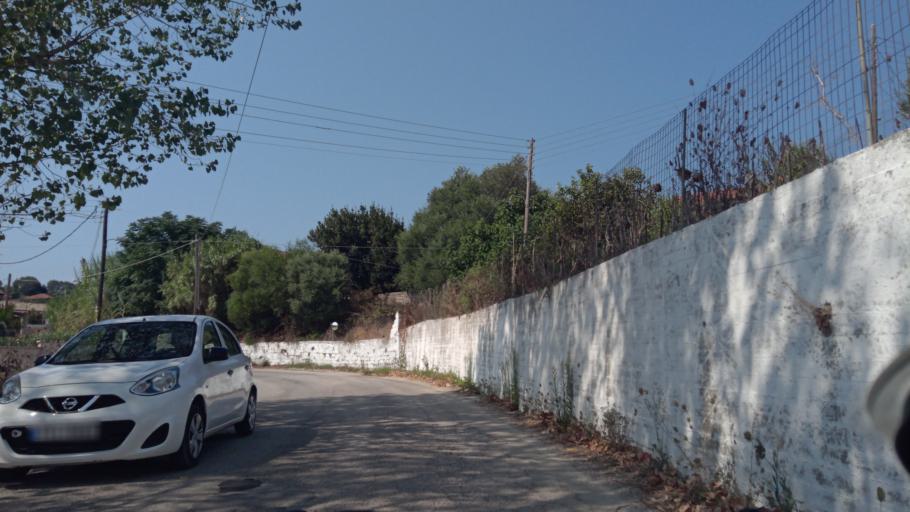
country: GR
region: Ionian Islands
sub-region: Nomos Kerkyras
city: Perivoli
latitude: 39.4121
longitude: 20.0232
